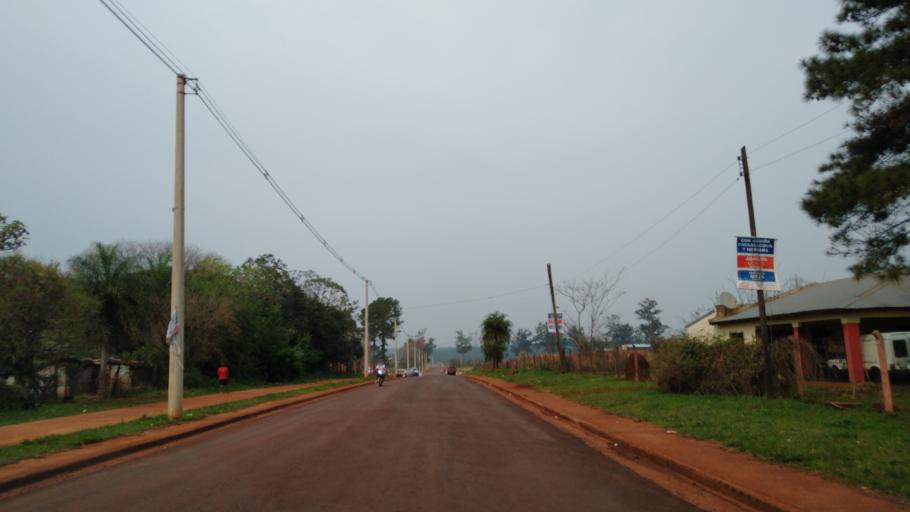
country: AR
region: Misiones
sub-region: Departamento de Capital
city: Posadas
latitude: -27.4444
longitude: -55.9331
